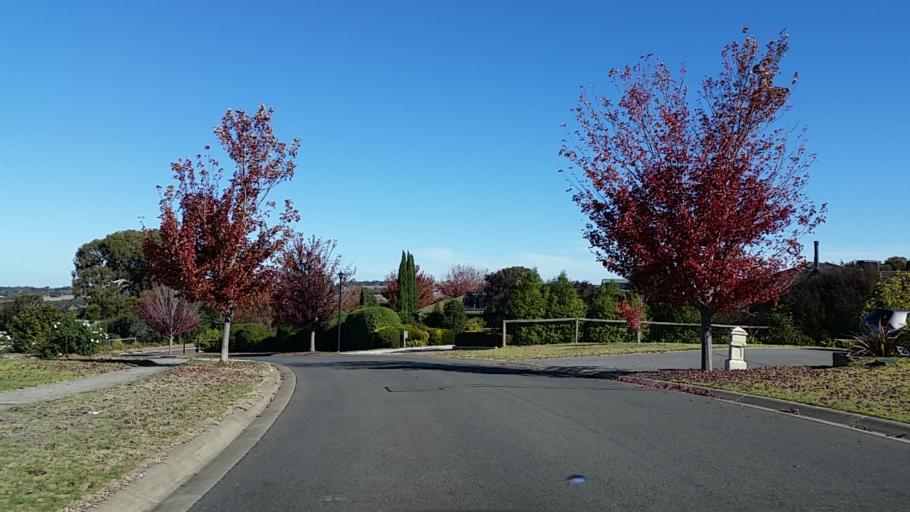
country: AU
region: South Australia
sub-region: Mount Barker
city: Mount Barker
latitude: -35.0619
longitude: 138.8856
